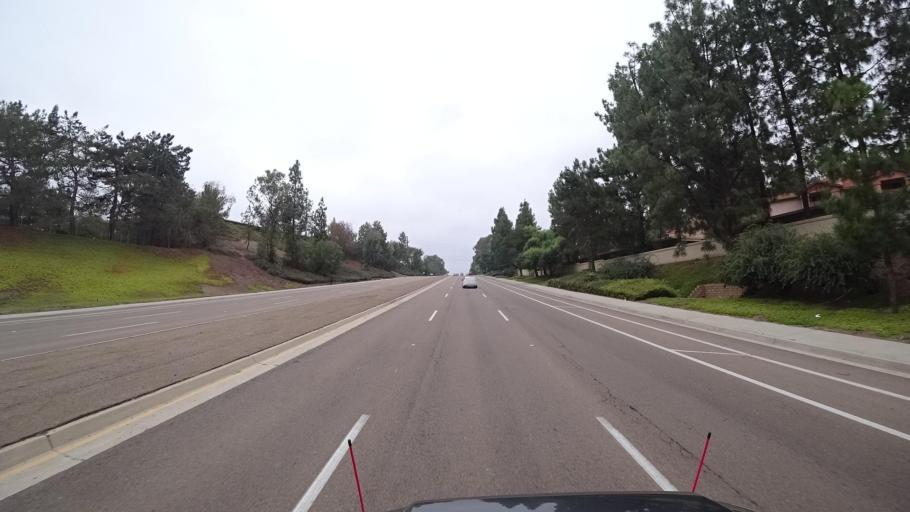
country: US
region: California
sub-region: San Diego County
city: Poway
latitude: 32.9921
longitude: -117.0740
